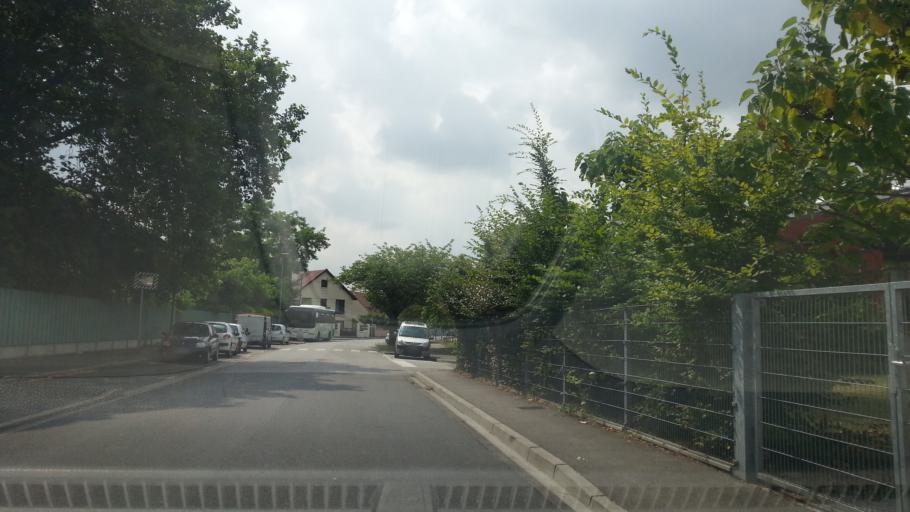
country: FR
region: Picardie
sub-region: Departement de l'Oise
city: Montataire
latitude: 49.2579
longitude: 2.4511
